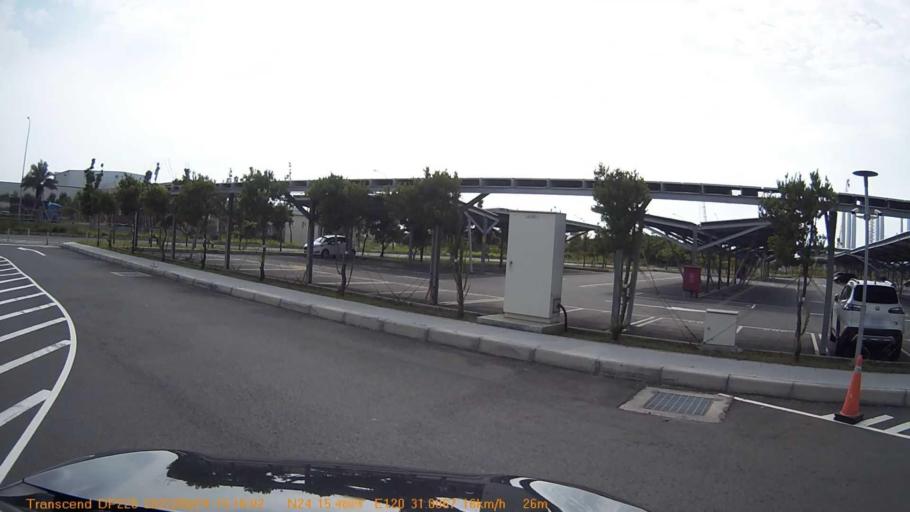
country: TW
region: Taiwan
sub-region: Changhua
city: Chang-hua
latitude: 24.2580
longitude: 120.5167
